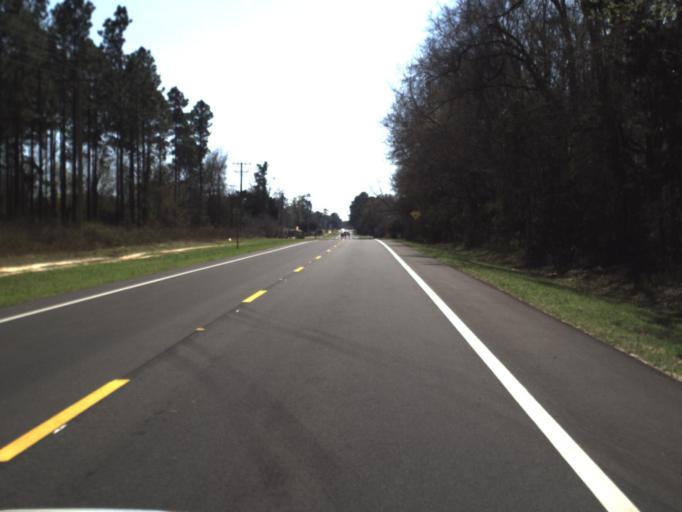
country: US
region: Florida
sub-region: Jackson County
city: Sneads
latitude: 30.7282
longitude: -85.0201
